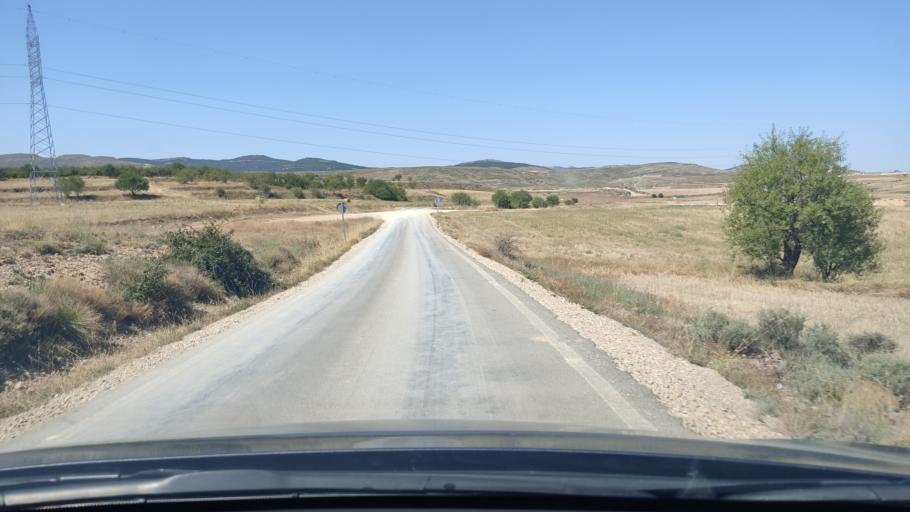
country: ES
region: Aragon
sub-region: Provincia de Teruel
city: Monforte de Moyuela
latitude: 41.0422
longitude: -0.9856
